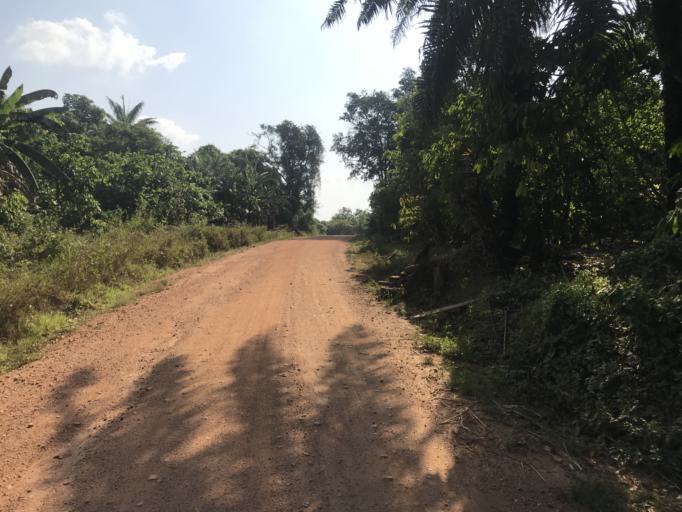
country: NG
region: Osun
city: Ikirun
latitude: 7.8723
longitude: 4.5856
